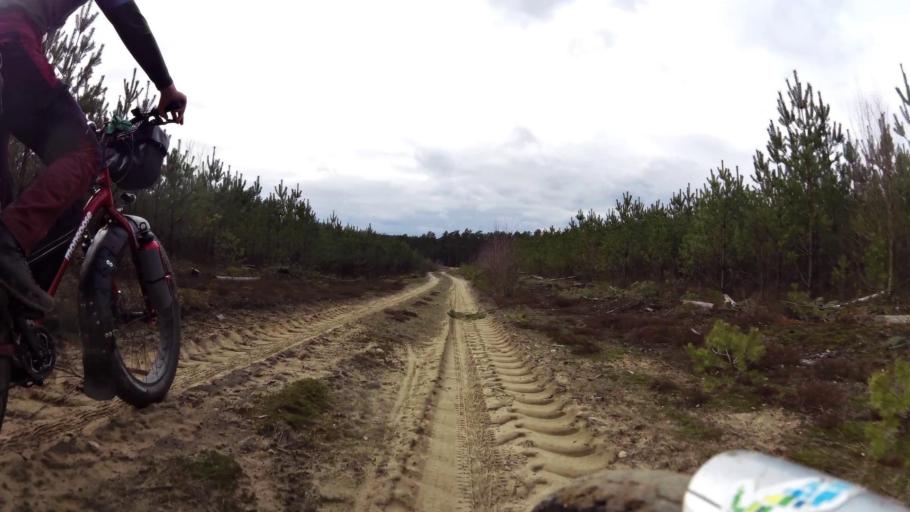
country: PL
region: Pomeranian Voivodeship
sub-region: Powiat bytowski
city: Trzebielino
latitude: 54.1508
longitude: 17.1647
